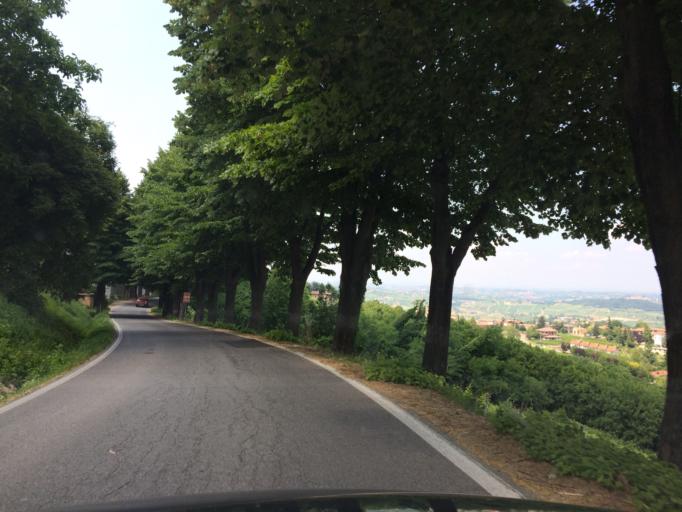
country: IT
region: Piedmont
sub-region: Provincia di Asti
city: Calosso
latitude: 44.7373
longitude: 8.2307
